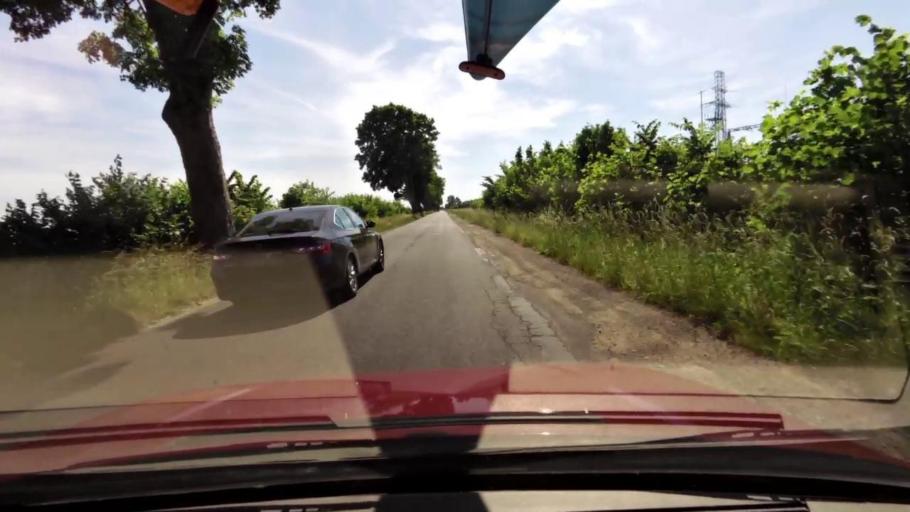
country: PL
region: Pomeranian Voivodeship
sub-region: Powiat slupski
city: Kobylnica
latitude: 54.4020
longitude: 16.9973
